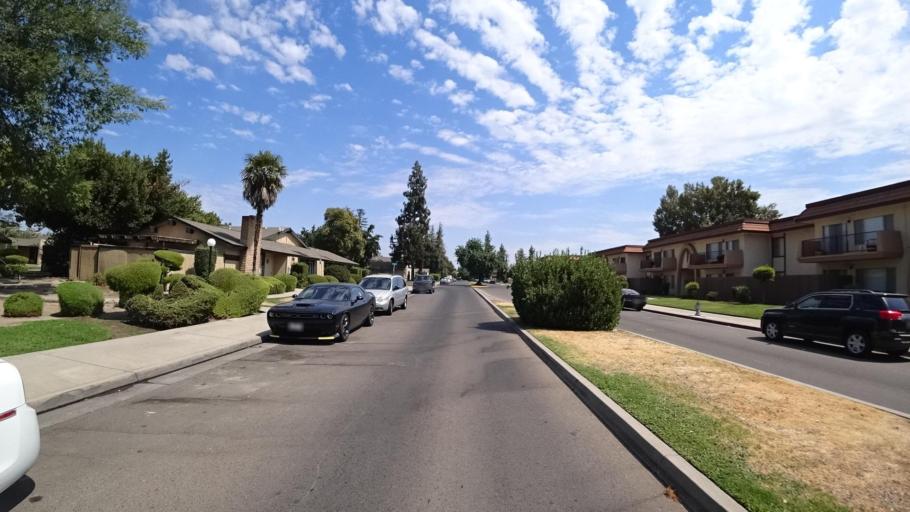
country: US
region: California
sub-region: Fresno County
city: Sunnyside
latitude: 36.7389
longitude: -119.6931
